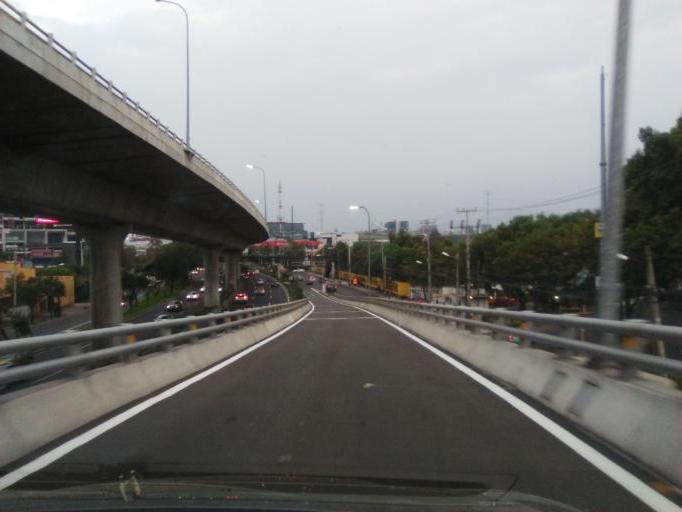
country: MX
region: Mexico City
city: Magdalena Contreras
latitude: 19.3095
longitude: -99.2181
